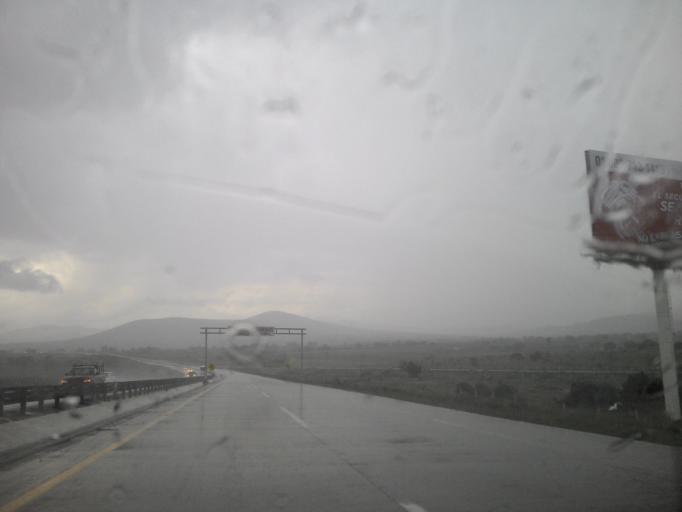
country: MX
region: Hidalgo
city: Zempoala
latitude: 19.8864
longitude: -98.6376
